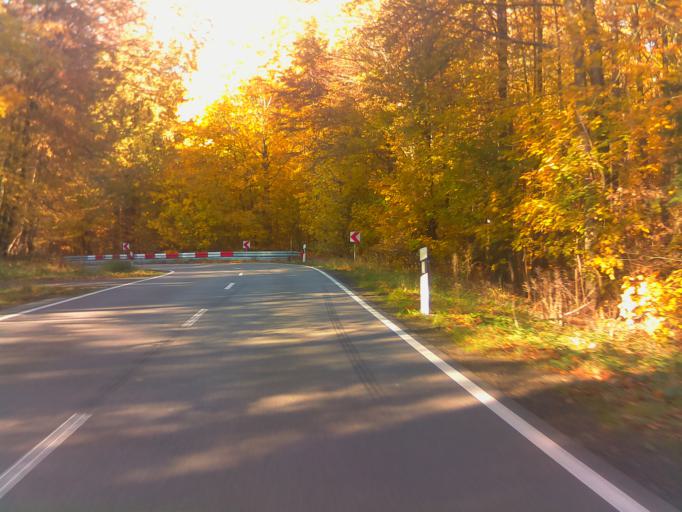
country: DE
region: Bavaria
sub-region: Regierungsbezirk Unterfranken
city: Knetzgau
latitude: 49.9283
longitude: 10.5642
